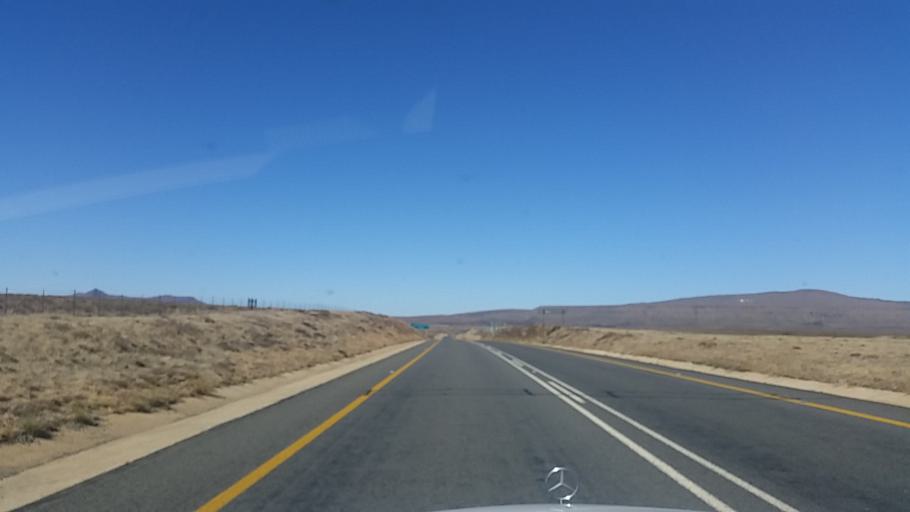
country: ZA
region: Eastern Cape
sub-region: Cacadu District Municipality
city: Graaff-Reinet
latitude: -31.9109
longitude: 24.7641
